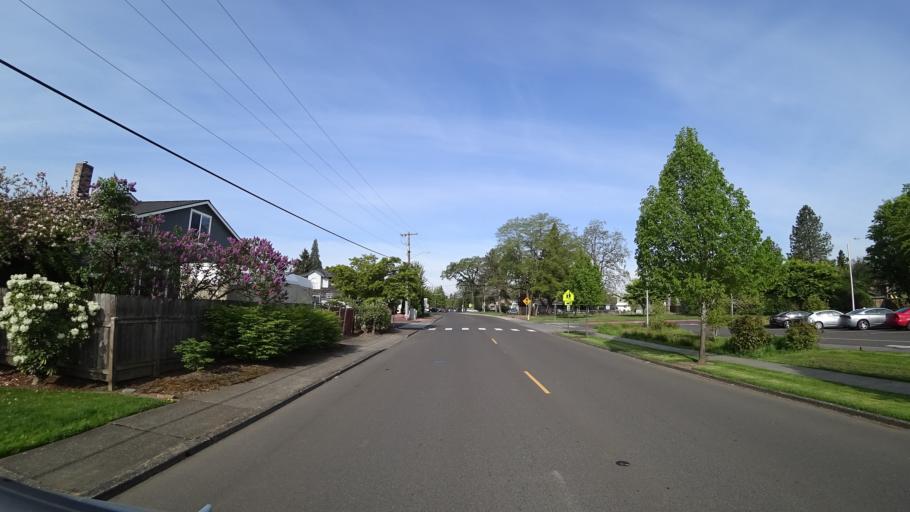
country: US
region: Oregon
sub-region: Washington County
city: Hillsboro
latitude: 45.5277
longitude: -122.9671
